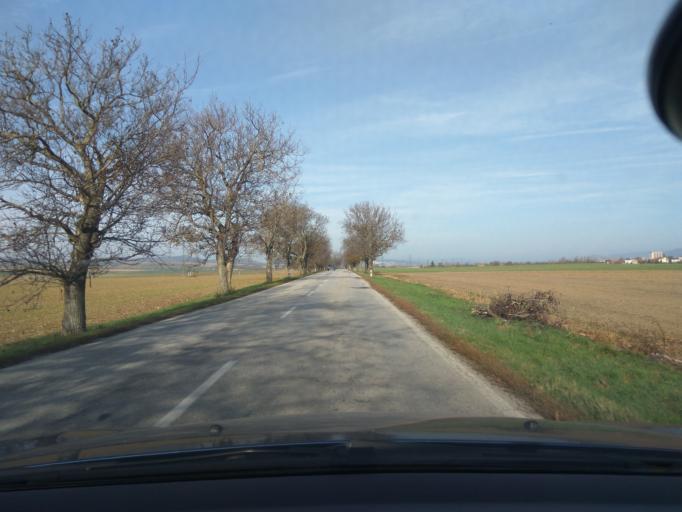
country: SK
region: Trnavsky
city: Vrbove
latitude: 48.6197
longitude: 17.7516
